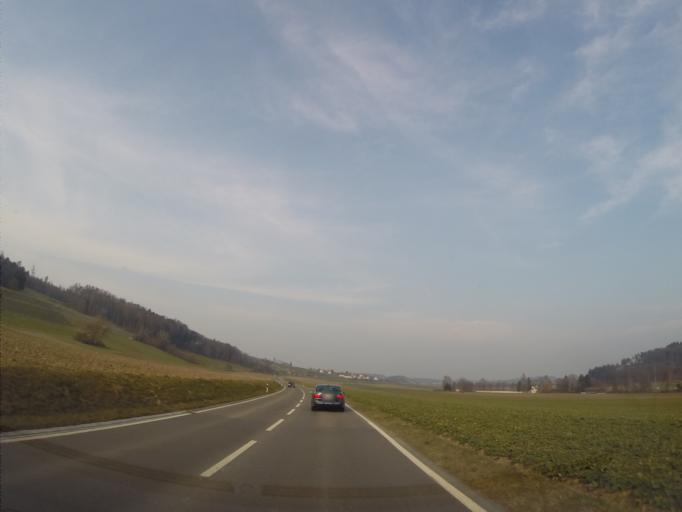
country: CH
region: Zurich
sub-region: Bezirk Winterthur
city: Neftenbach / Dorf Neftenbach
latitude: 47.5318
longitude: 8.6671
